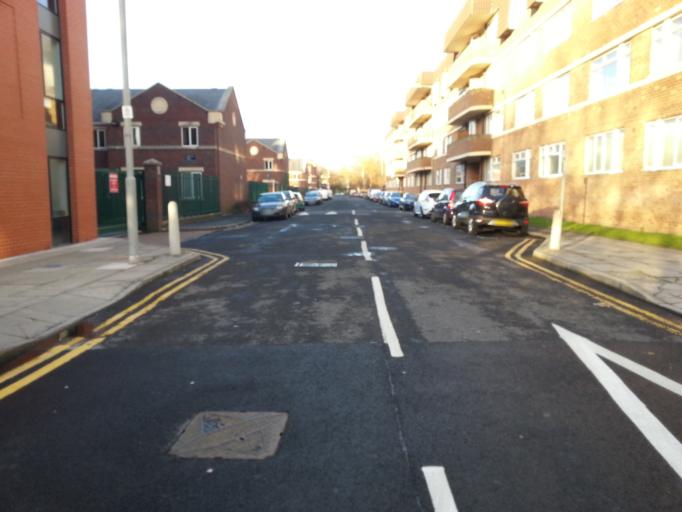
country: GB
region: England
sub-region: Liverpool
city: Liverpool
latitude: 53.4007
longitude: -2.9613
